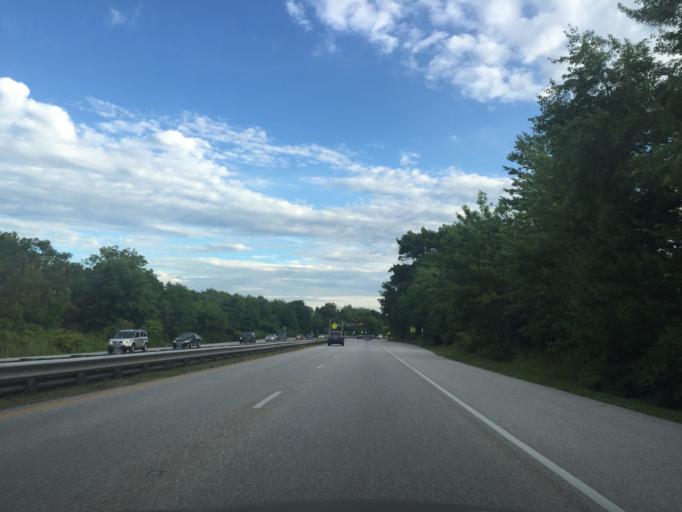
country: US
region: Maryland
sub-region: Baltimore County
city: Parkville
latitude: 39.3915
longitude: -76.5507
